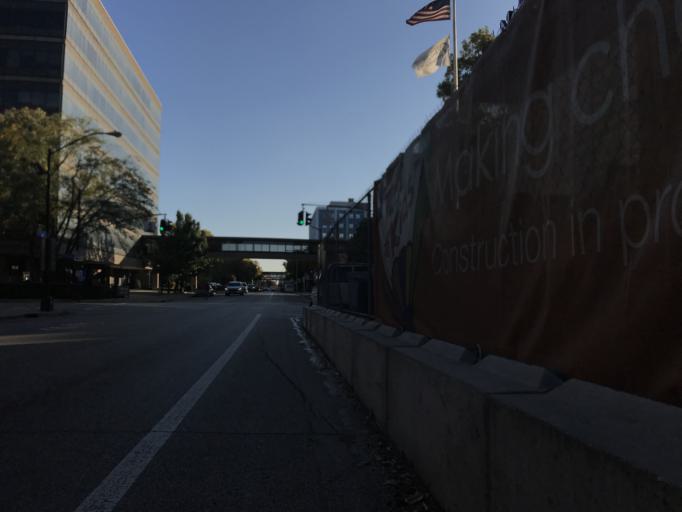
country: US
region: Kentucky
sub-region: Jefferson County
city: Louisville
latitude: 38.2484
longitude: -85.7493
